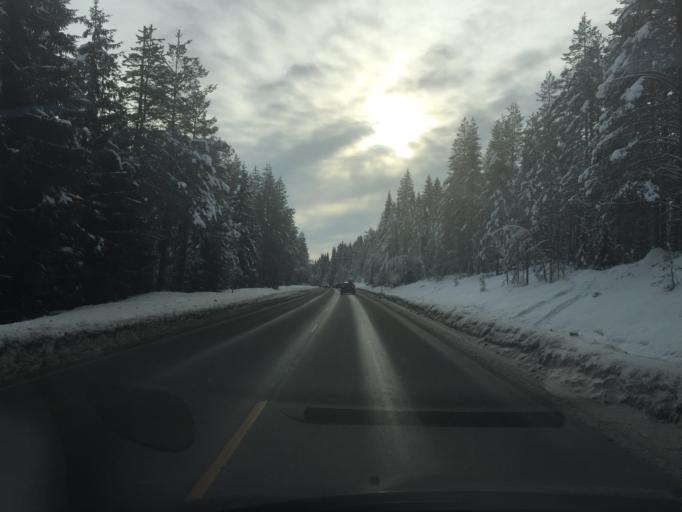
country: NO
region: Hedmark
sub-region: Trysil
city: Innbygda
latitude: 61.2806
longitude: 12.2843
